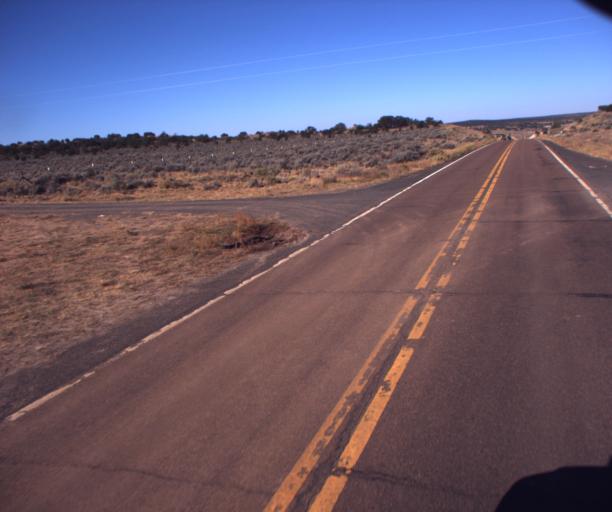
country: US
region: Arizona
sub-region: Apache County
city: Ganado
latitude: 35.7582
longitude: -109.9612
